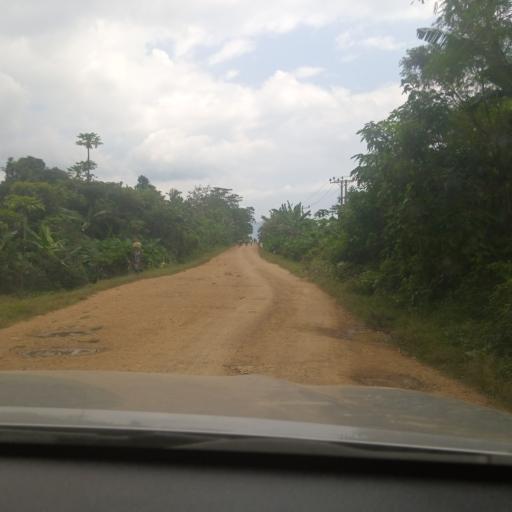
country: ET
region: Southern Nations, Nationalities, and People's Region
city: Tippi
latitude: 7.1367
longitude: 35.4228
